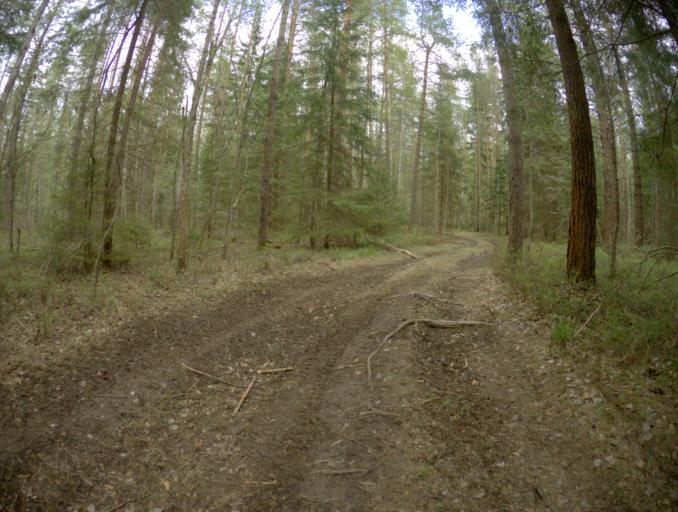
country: RU
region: Vladimir
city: Golovino
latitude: 55.9153
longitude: 40.5000
